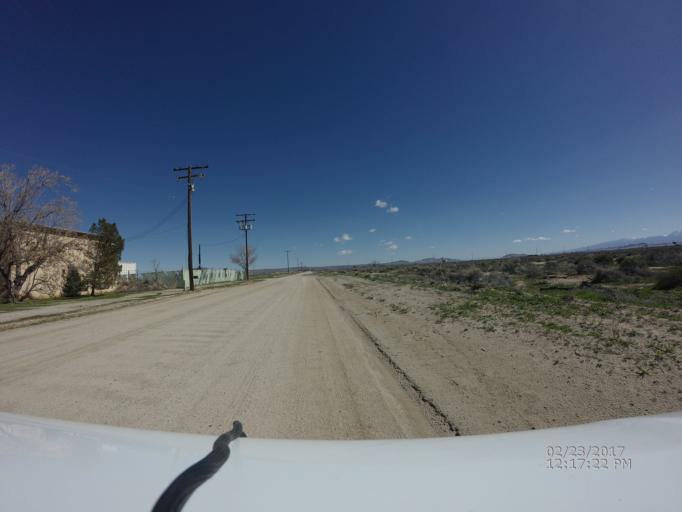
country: US
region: California
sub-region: Los Angeles County
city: Lancaster
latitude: 34.7415
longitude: -117.9761
